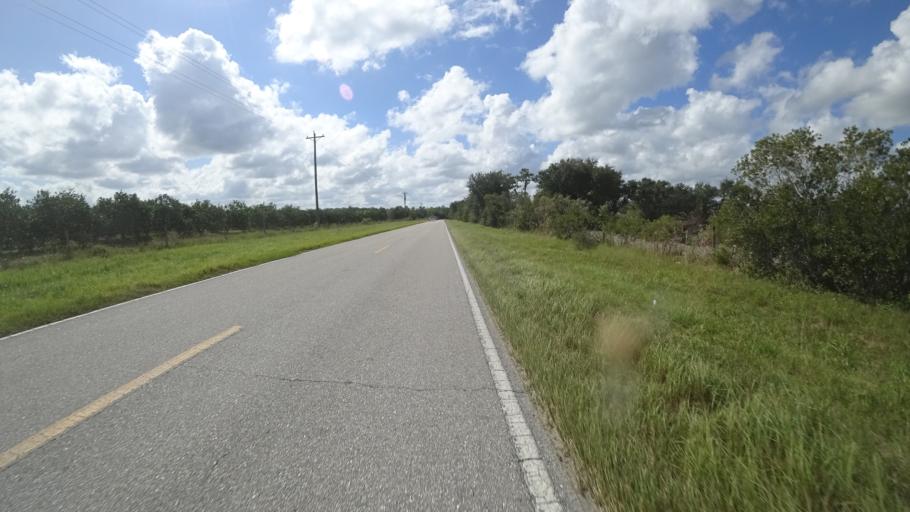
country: US
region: Florida
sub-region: Sarasota County
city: Lake Sarasota
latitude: 27.3931
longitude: -82.1338
